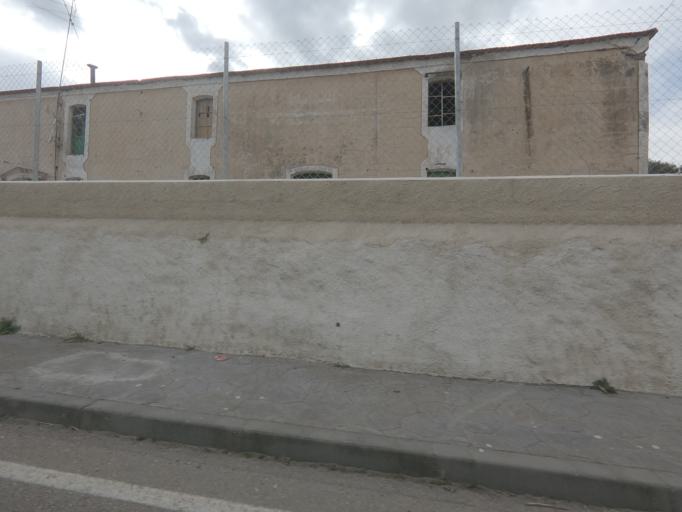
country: ES
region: Castille and Leon
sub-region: Provincia de Salamanca
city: Robleda
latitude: 40.3838
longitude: -6.6103
